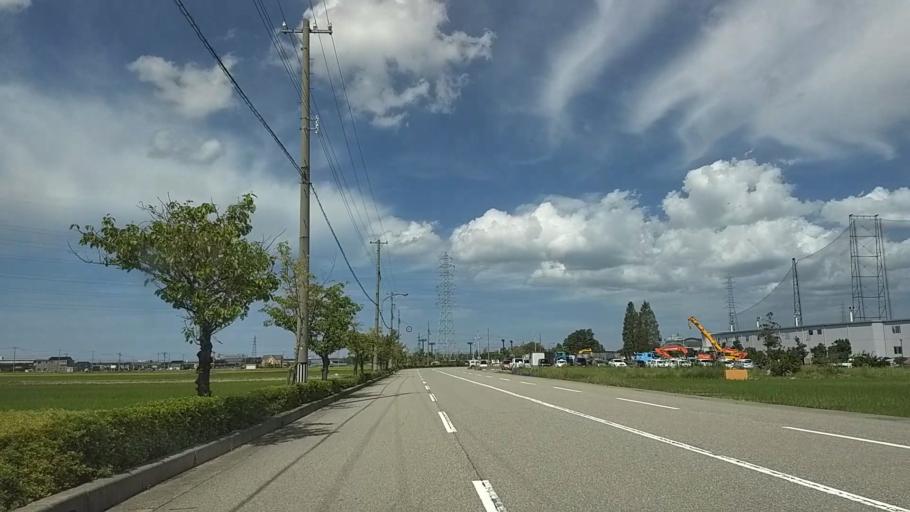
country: JP
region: Ishikawa
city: Kanazawa-shi
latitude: 36.5910
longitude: 136.6563
